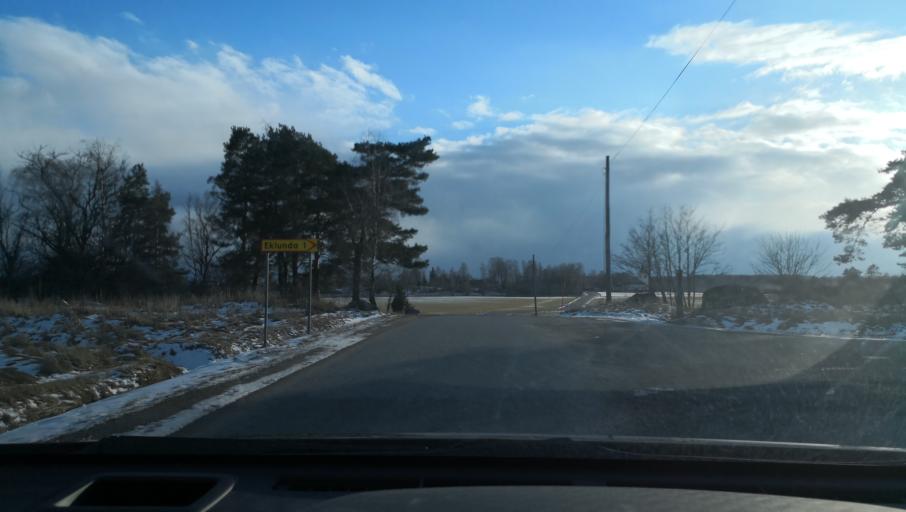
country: SE
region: Uppsala
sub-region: Enkopings Kommun
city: Irsta
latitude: 59.6879
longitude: 16.8578
